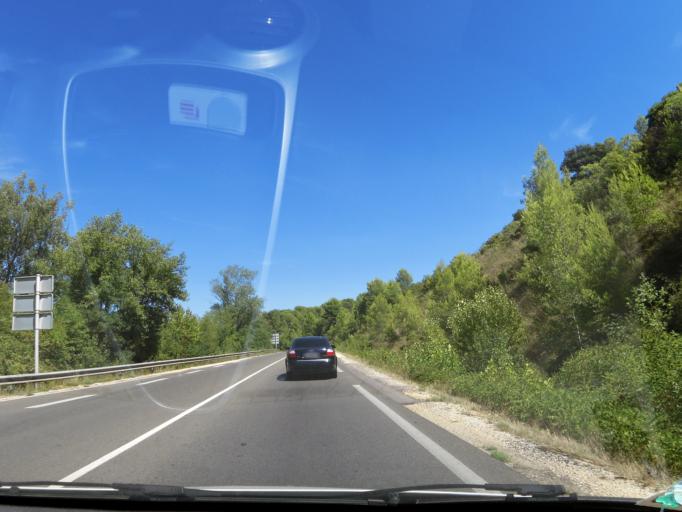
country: FR
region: Languedoc-Roussillon
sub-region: Departement de l'Herault
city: Castelnau-le-Lez
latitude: 43.6445
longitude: 3.9004
